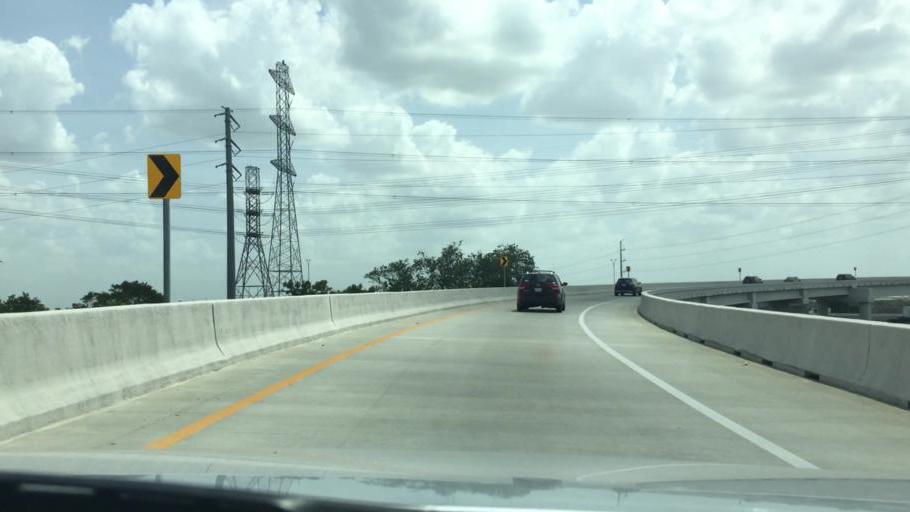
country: US
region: Texas
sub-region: Harris County
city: Hudson
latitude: 29.9393
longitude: -95.5211
